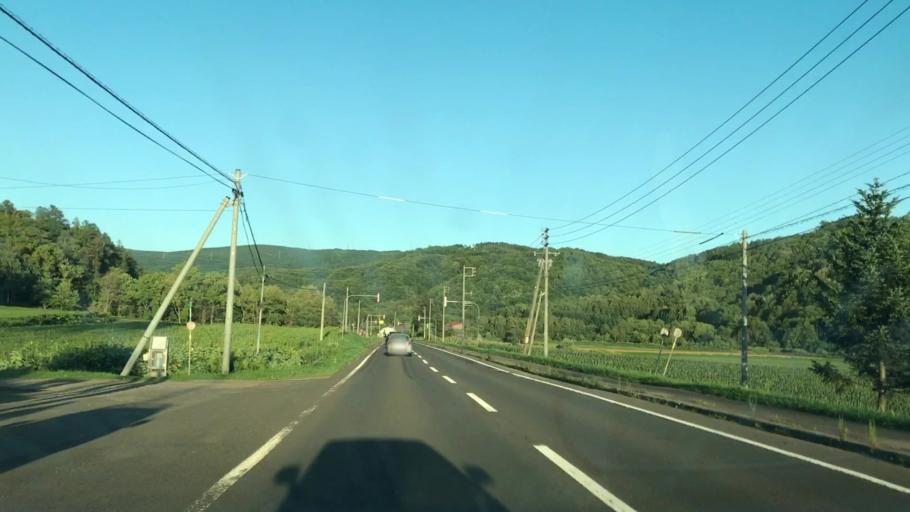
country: JP
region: Hokkaido
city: Niseko Town
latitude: 42.8006
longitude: 140.9749
